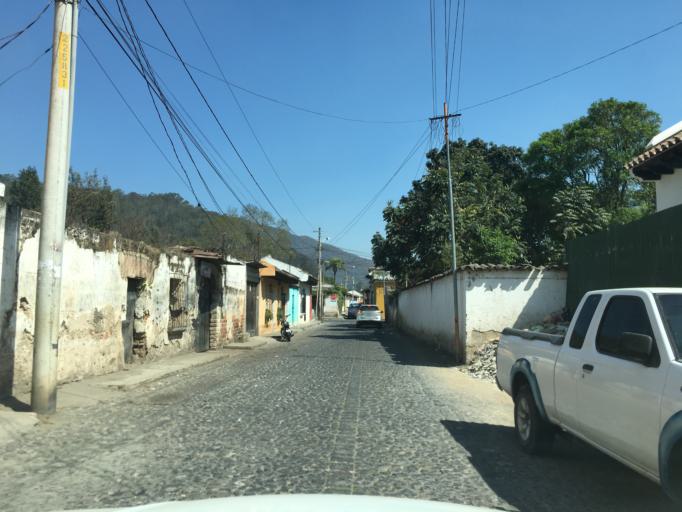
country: GT
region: Sacatepequez
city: Antigua Guatemala
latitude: 14.5628
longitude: -90.7379
